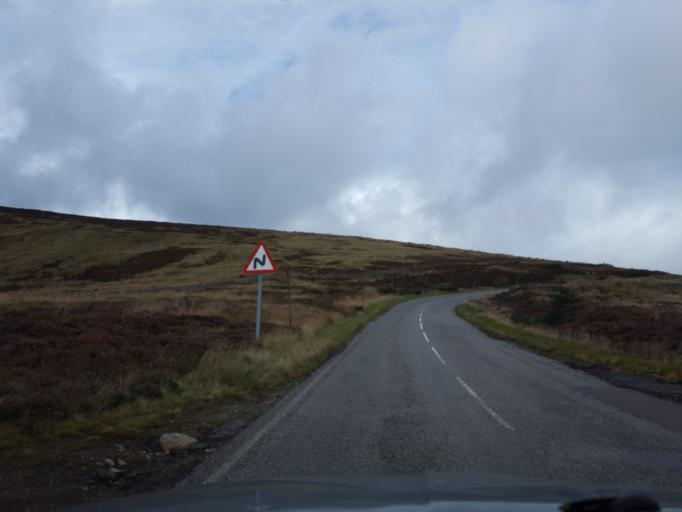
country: GB
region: Scotland
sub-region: Aberdeenshire
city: Laurencekirk
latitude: 56.9105
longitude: -2.5732
